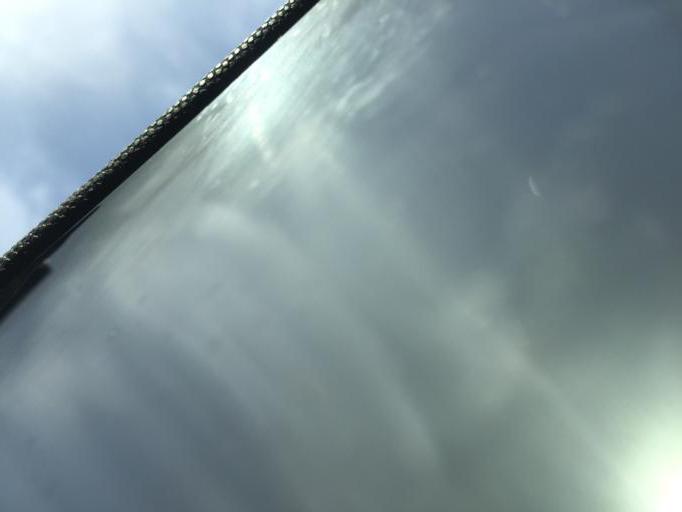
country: GB
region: England
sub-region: Oxfordshire
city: Bloxham
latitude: 52.0257
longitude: -1.3892
